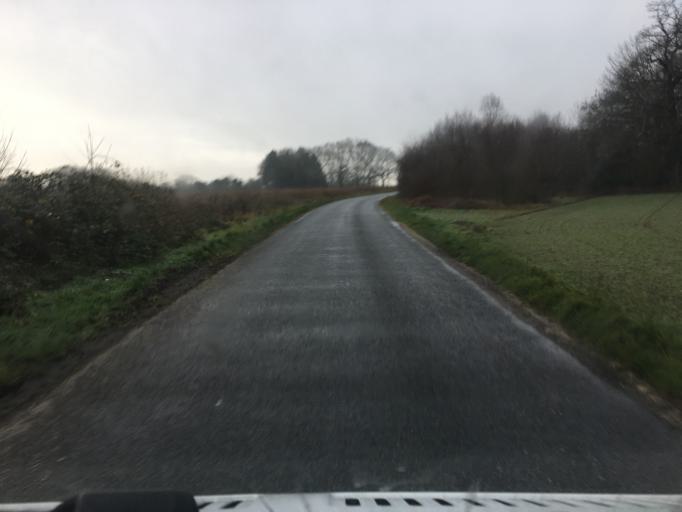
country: FR
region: Picardie
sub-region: Departement de la Somme
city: Saint-Valery-sur-Somme
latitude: 50.1786
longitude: 1.6256
